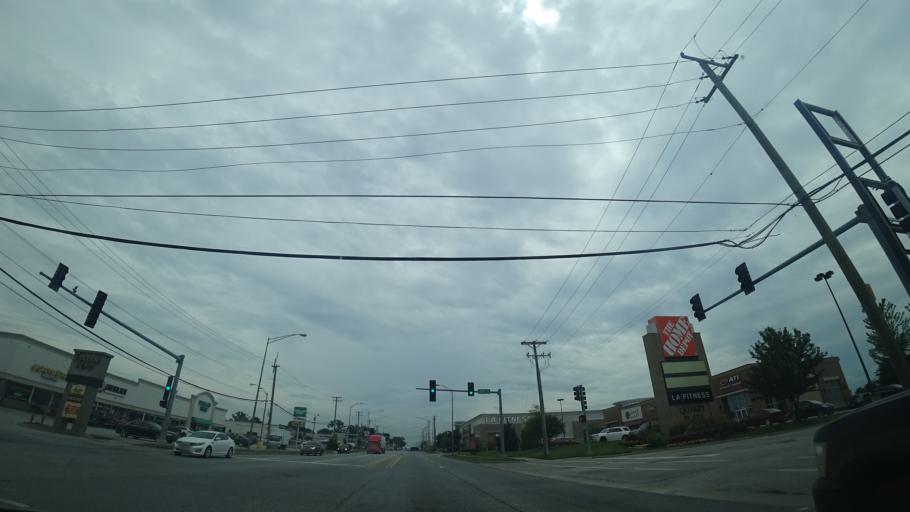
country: US
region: Illinois
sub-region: Cook County
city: Alsip
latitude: 41.6745
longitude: -87.7391
